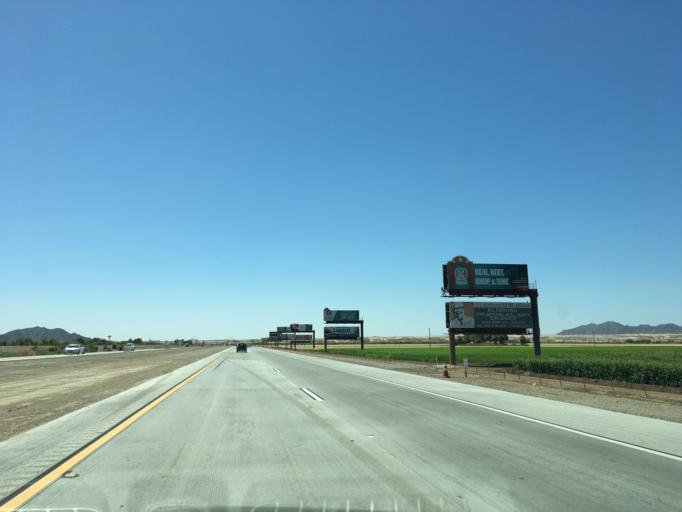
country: US
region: Arizona
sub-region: Yuma County
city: Yuma
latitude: 32.7385
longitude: -114.6666
